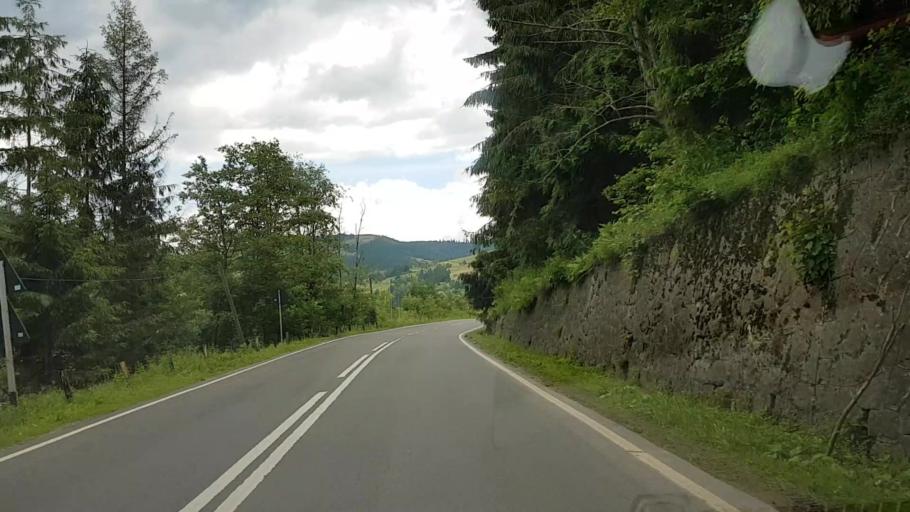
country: RO
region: Neamt
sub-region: Comuna Poiana Teiului
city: Poiana Teiului
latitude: 47.0925
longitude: 25.9530
